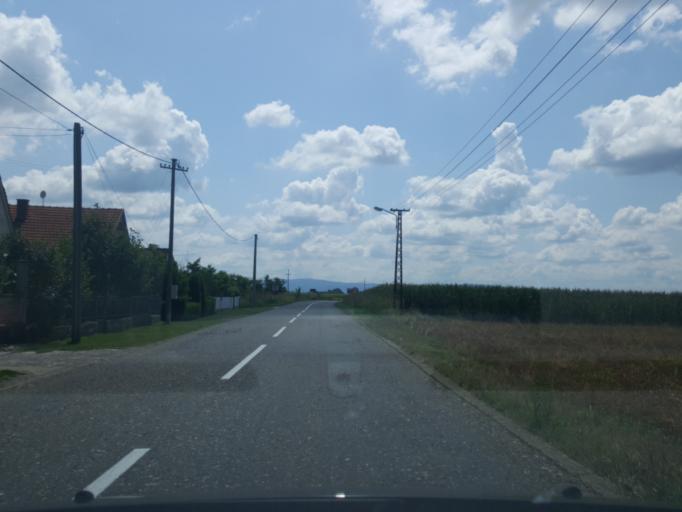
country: RS
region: Central Serbia
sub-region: Macvanski Okrug
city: Bogatic
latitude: 44.8106
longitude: 19.4756
